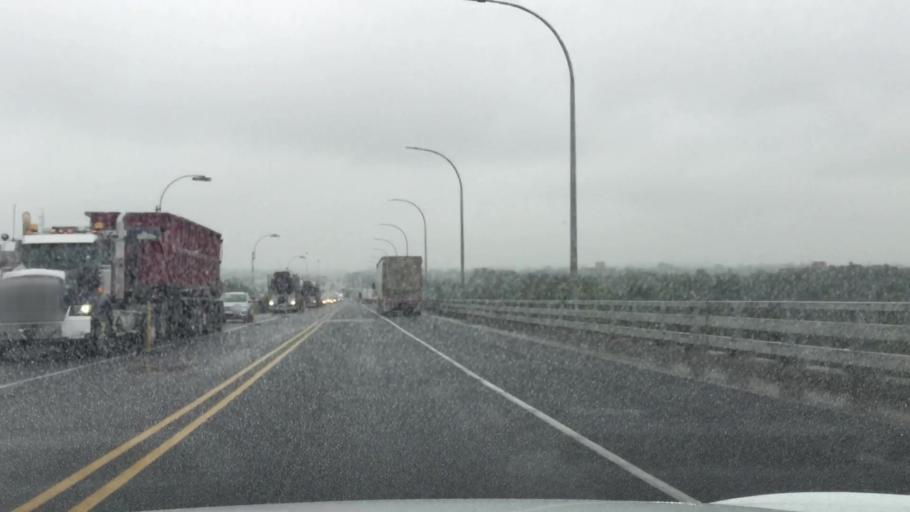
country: US
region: Michigan
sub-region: Wayne County
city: Detroit
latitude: 42.3070
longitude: -83.0709
